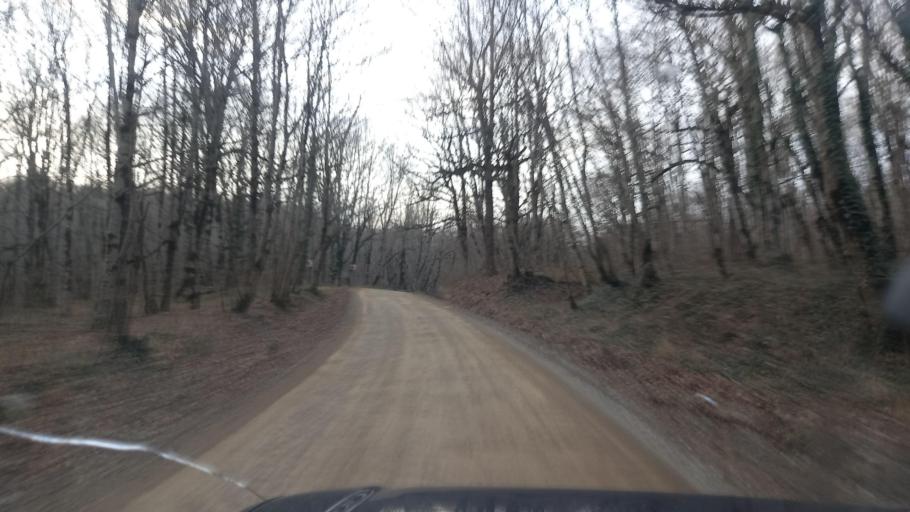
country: RU
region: Krasnodarskiy
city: Agoy
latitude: 44.3431
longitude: 39.2434
